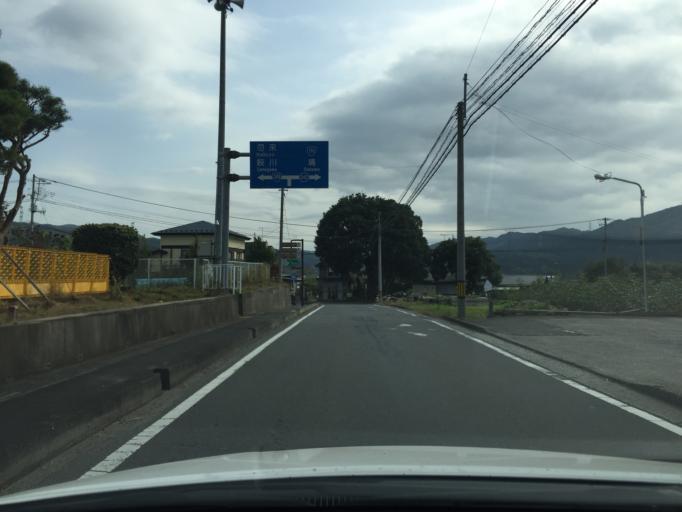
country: JP
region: Fukushima
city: Ishikawa
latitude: 36.9674
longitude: 140.4332
